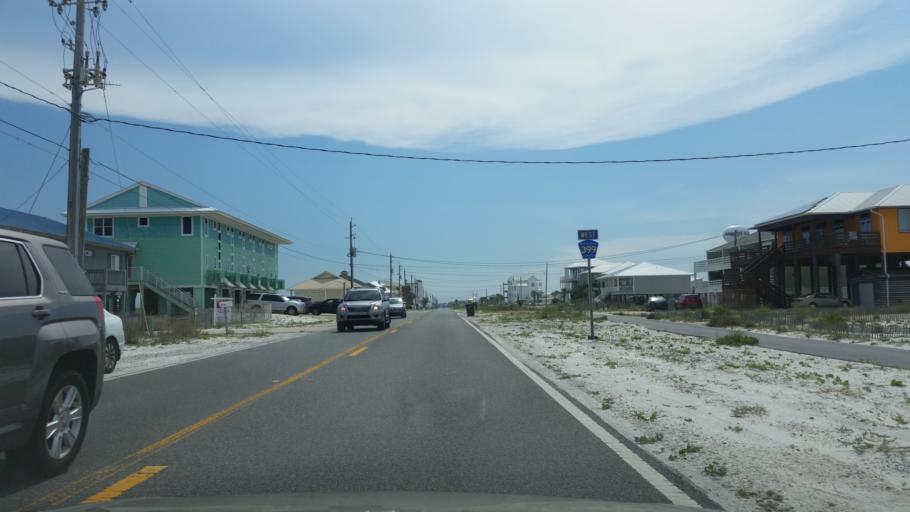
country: US
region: Florida
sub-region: Santa Rosa County
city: Navarre
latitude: 30.3778
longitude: -86.8806
